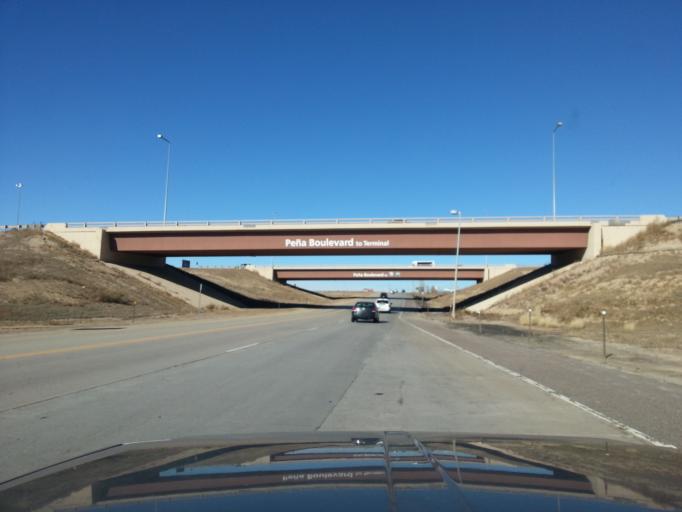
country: US
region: Colorado
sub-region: Adams County
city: Aurora
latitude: 39.8330
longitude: -104.7155
